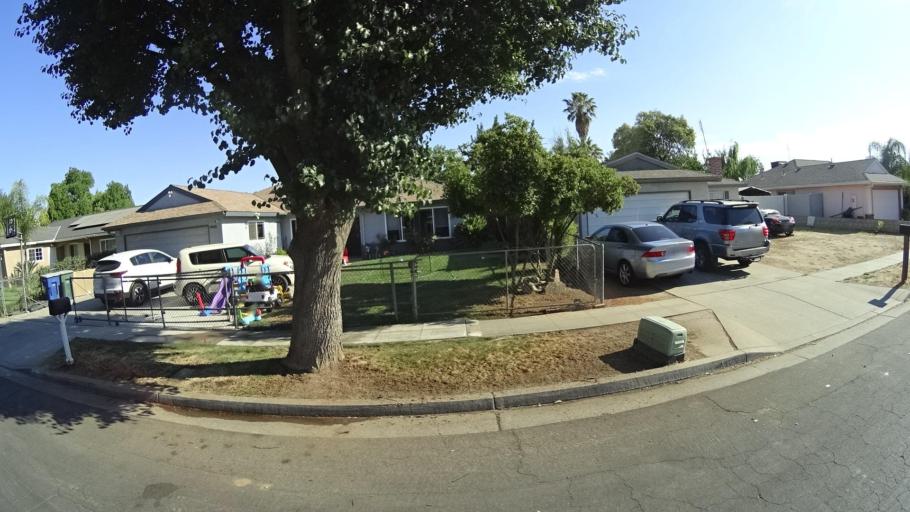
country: US
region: California
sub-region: Fresno County
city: Fresno
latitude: 36.7090
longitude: -119.7435
